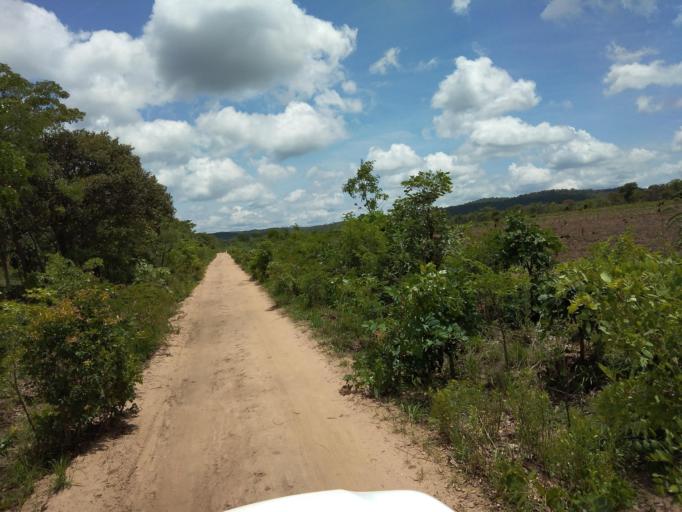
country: ZM
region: Central
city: Mkushi
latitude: -13.8922
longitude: 29.8456
